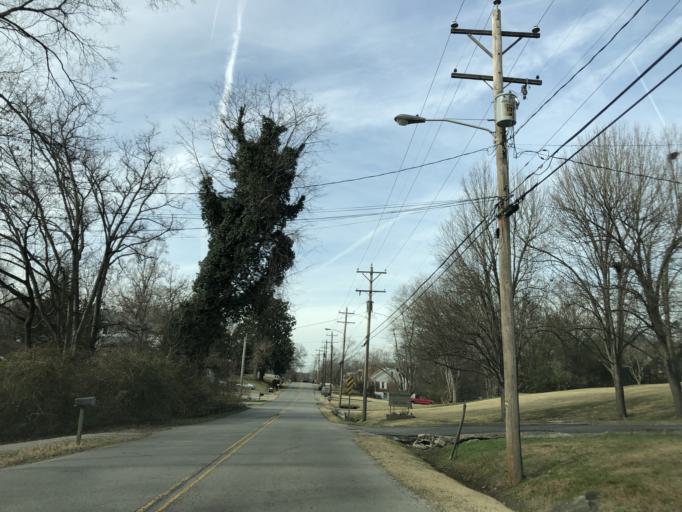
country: US
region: Tennessee
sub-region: Davidson County
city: Nashville
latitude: 36.2161
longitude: -86.7208
